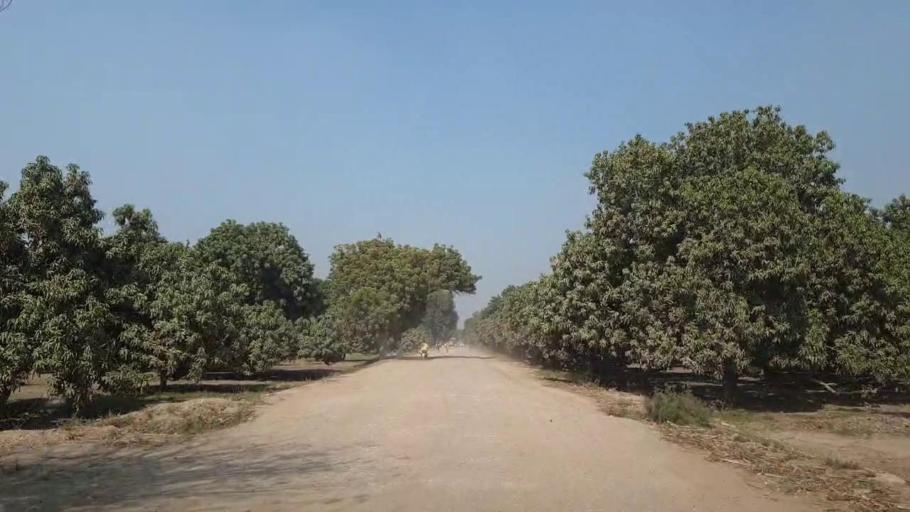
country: PK
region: Sindh
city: Tando Allahyar
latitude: 25.4869
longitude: 68.8226
